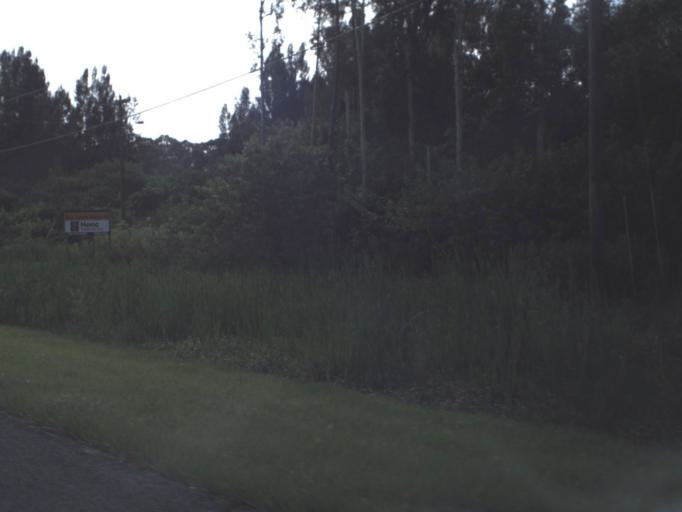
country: US
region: Florida
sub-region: Lee County
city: Pine Island Center
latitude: 26.6373
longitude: -82.0350
